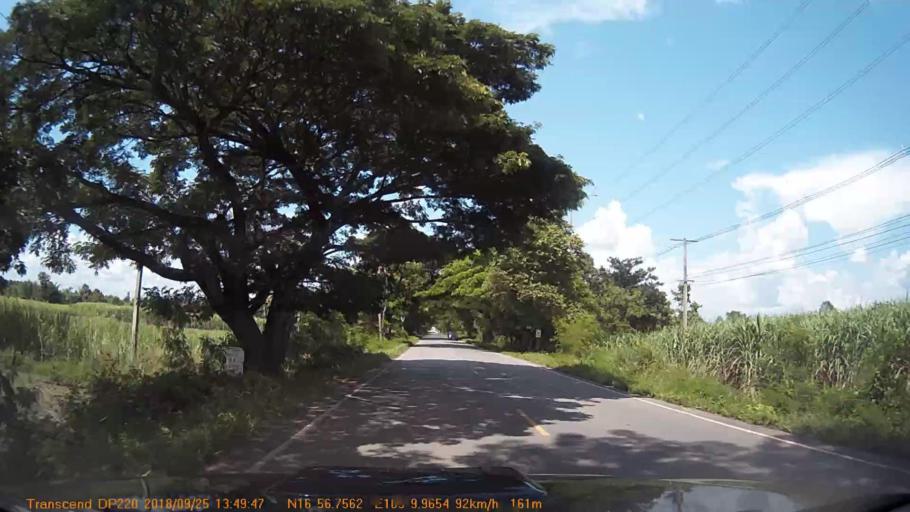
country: TH
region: Changwat Udon Thani
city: Si That
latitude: 16.9460
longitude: 103.1661
